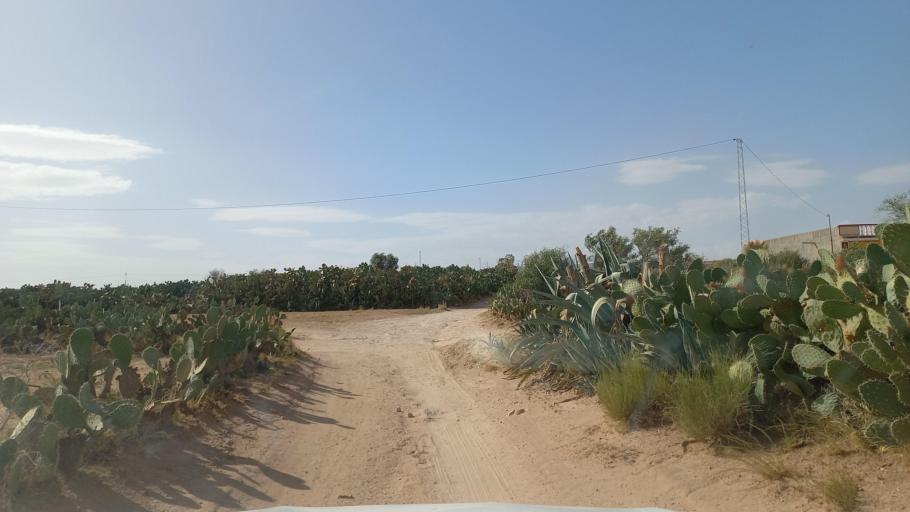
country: TN
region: Al Qasrayn
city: Kasserine
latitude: 35.2789
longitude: 8.9452
